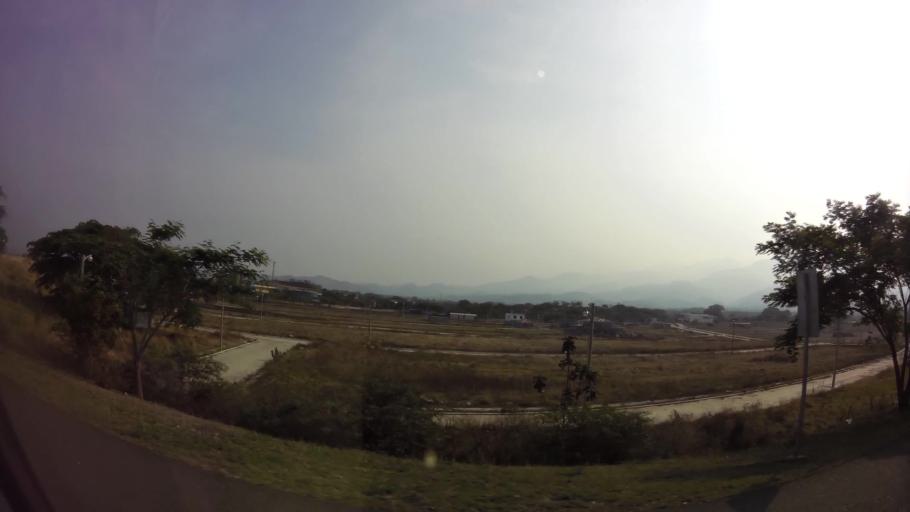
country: HN
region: Comayagua
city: Comayagua
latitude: 14.4257
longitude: -87.6344
